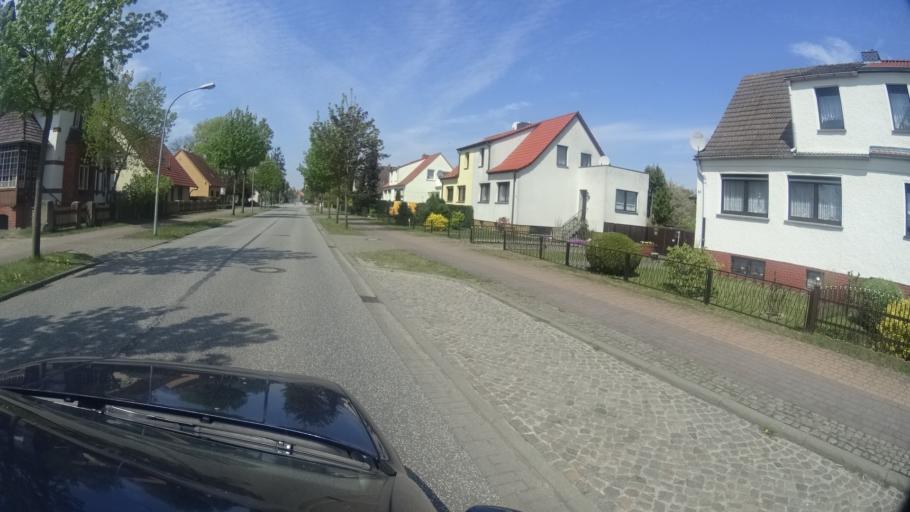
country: DE
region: Brandenburg
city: Wusterhausen
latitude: 52.8566
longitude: 12.4408
